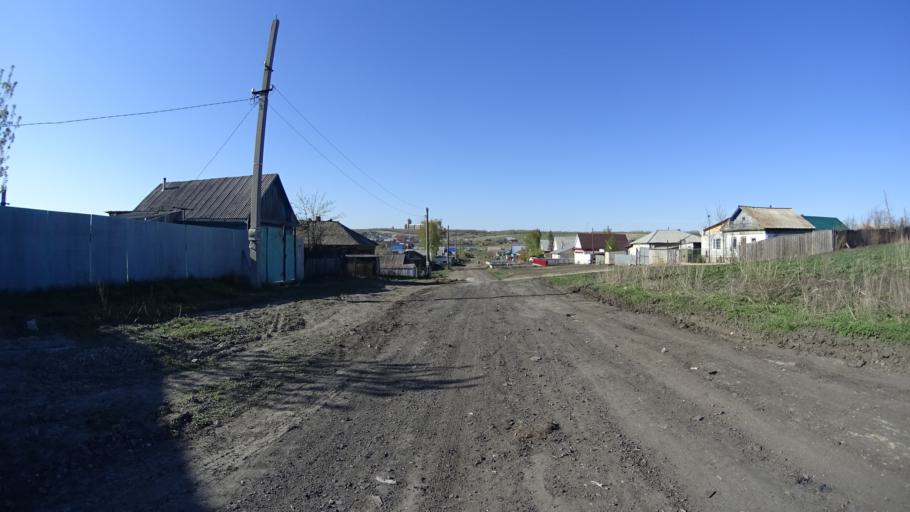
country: RU
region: Chelyabinsk
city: Troitsk
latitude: 54.0901
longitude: 61.6000
